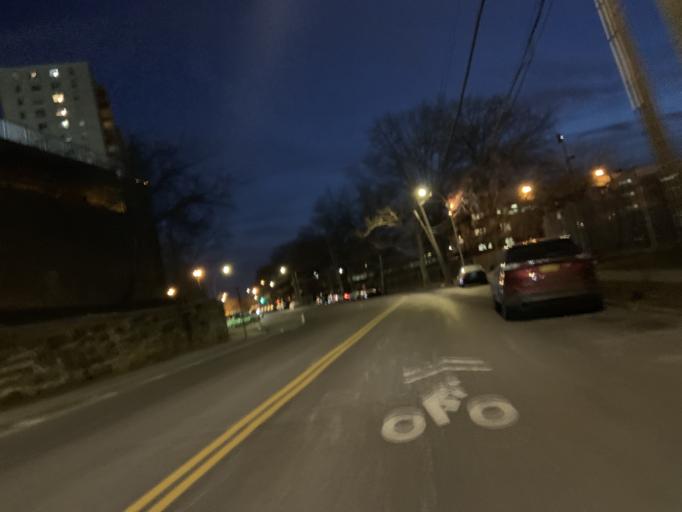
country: US
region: New York
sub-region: Bronx
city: The Bronx
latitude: 40.8787
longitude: -73.8888
